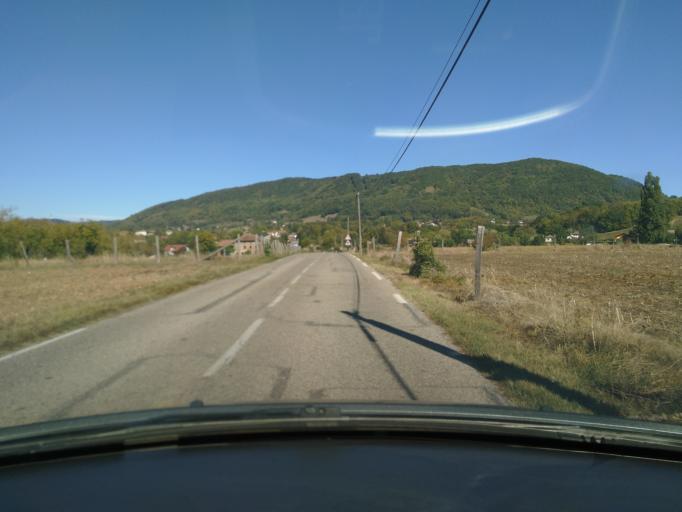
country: FR
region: Rhone-Alpes
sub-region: Departement de l'Isere
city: Saint-Cassien
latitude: 45.3641
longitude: 5.5534
